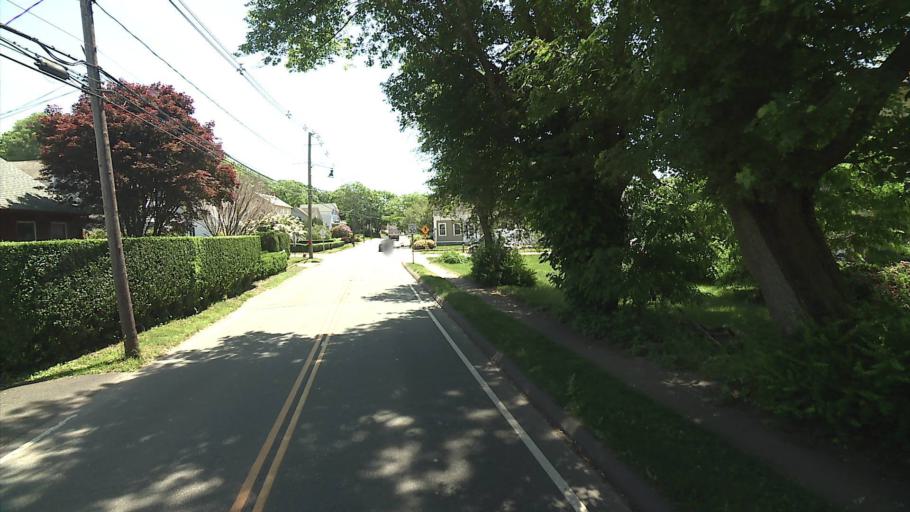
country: US
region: Connecticut
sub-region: New London County
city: Mystic
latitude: 41.3546
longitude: -71.9620
